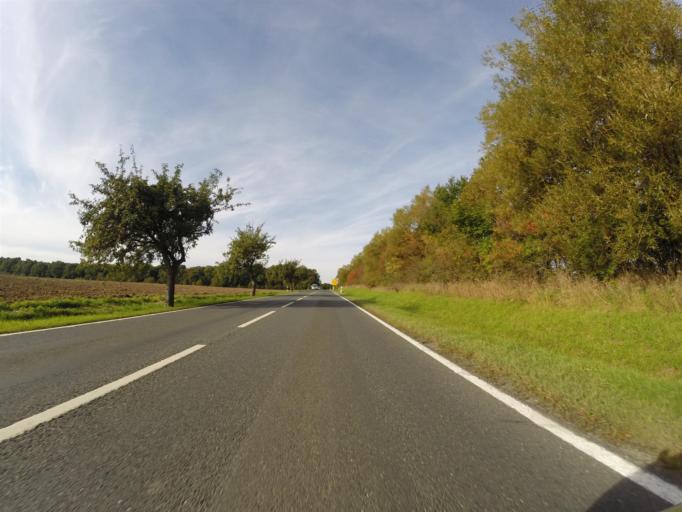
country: DE
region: Thuringia
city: Grossschwabhausen
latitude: 50.9681
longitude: 11.5239
